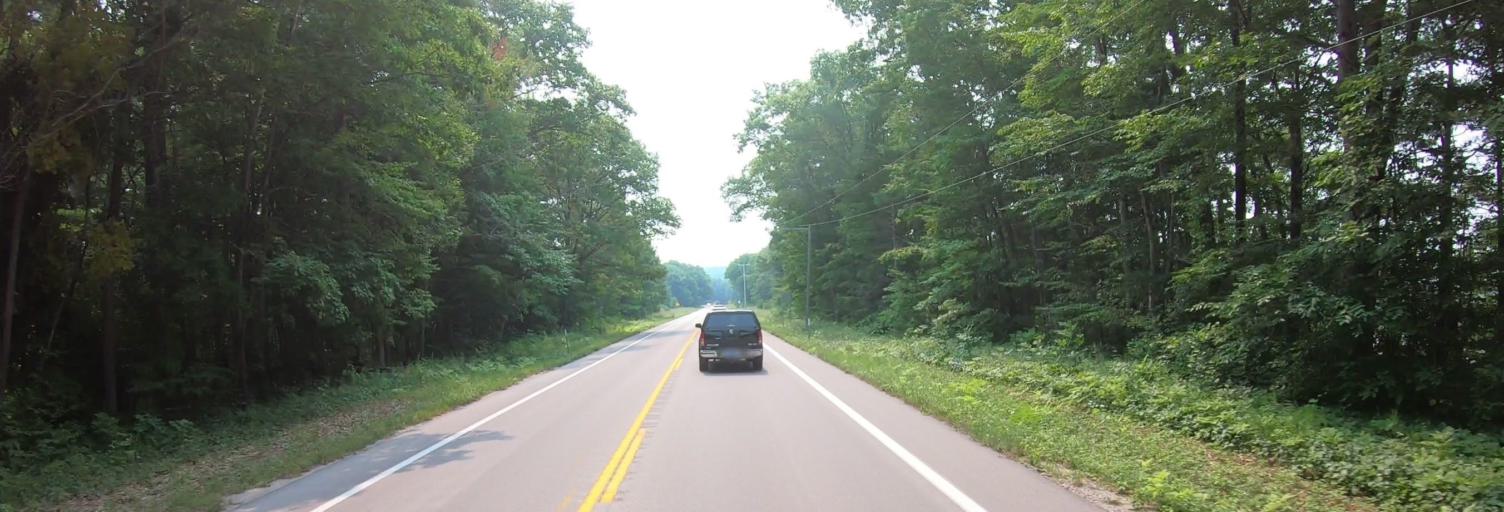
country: US
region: Michigan
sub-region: Leelanau County
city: Leland
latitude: 44.9271
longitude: -85.8827
